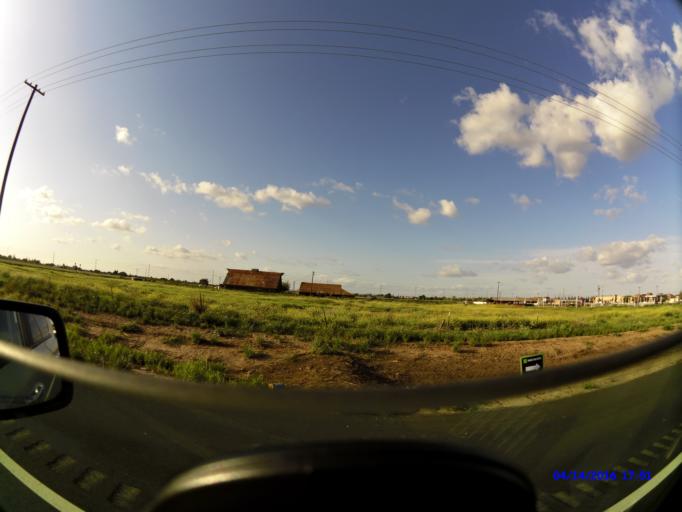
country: US
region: California
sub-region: Stanislaus County
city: Riverbank
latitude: 37.7112
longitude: -120.9608
